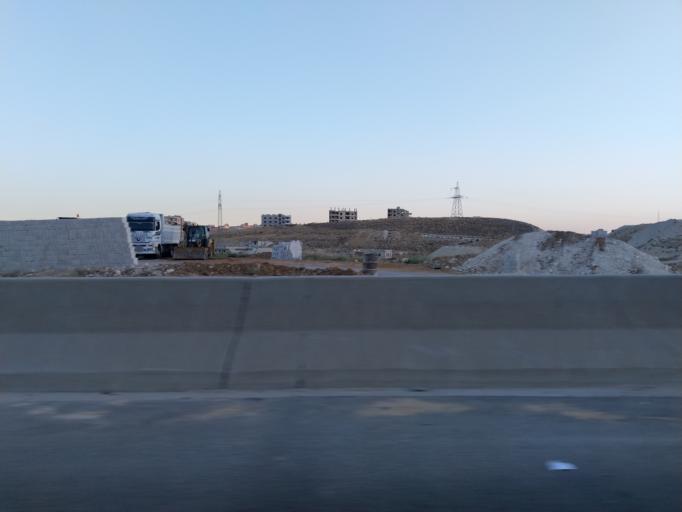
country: SY
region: Rif-dimashq
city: At Tall
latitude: 33.5862
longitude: 36.2978
